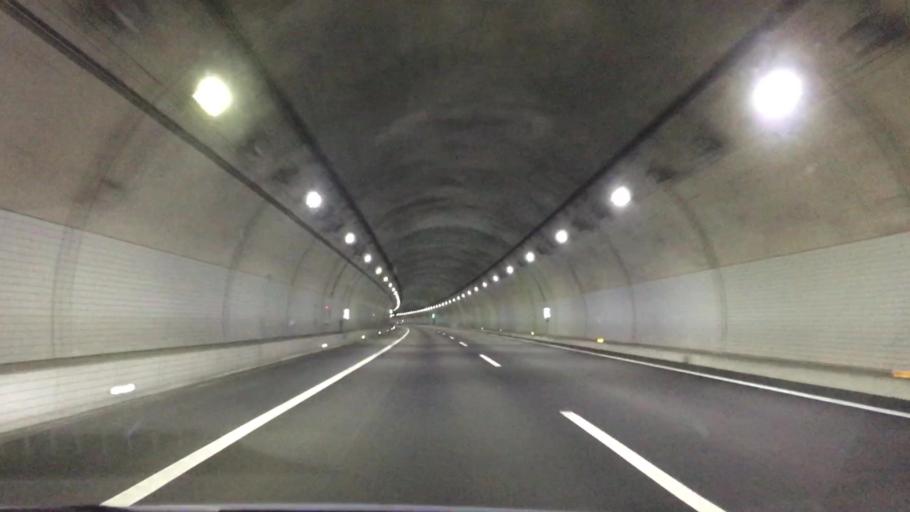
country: JP
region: Aichi
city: Shinshiro
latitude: 34.8532
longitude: 137.6173
